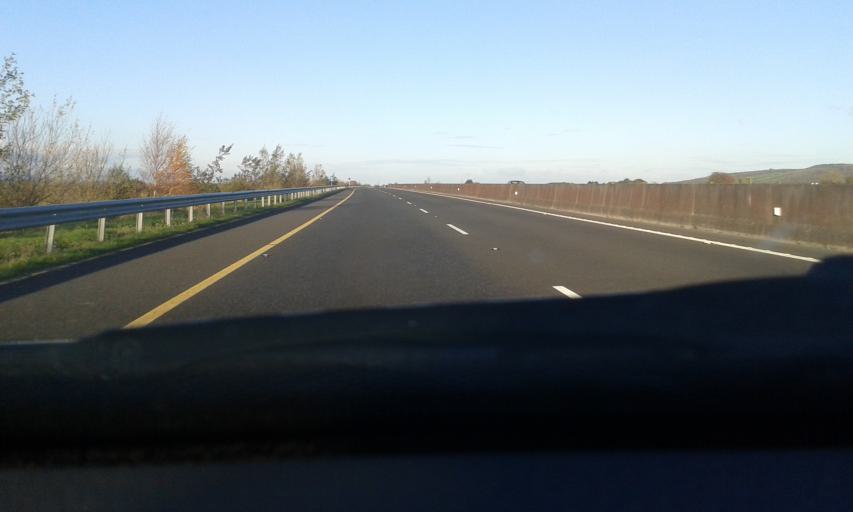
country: IE
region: Leinster
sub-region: Laois
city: Rathdowney
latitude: 52.7730
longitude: -7.5419
